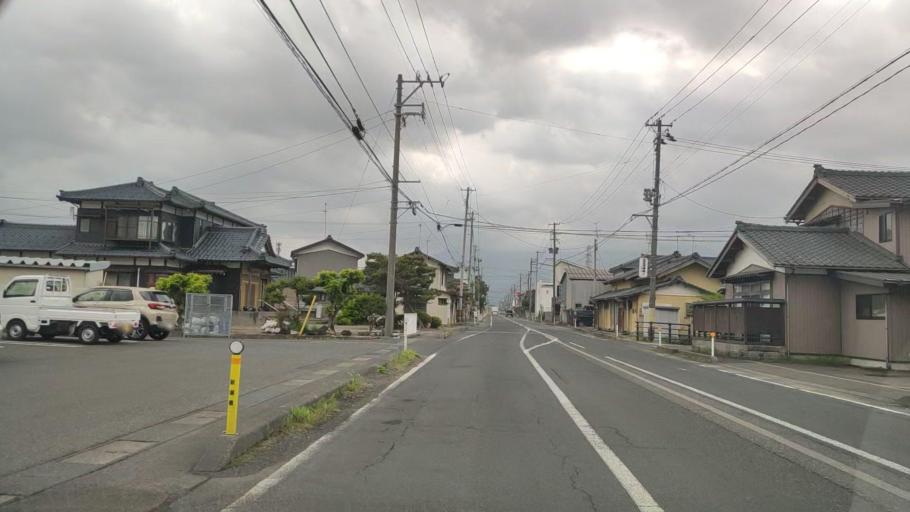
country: JP
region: Niigata
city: Gosen
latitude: 37.7358
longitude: 139.1906
